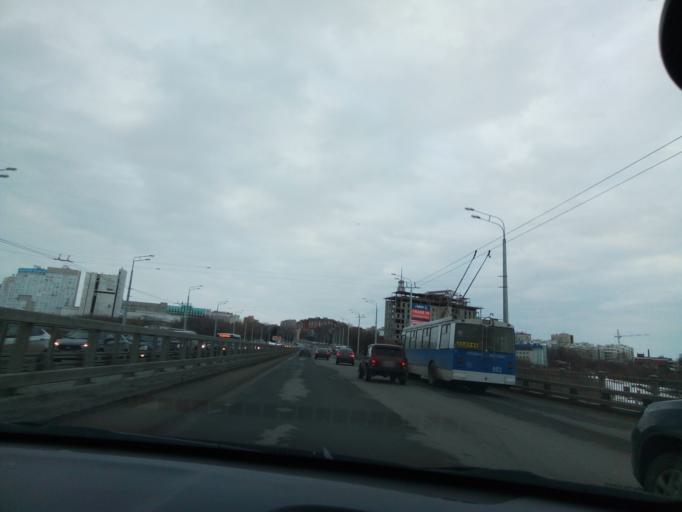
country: RU
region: Chuvashia
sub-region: Cheboksarskiy Rayon
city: Cheboksary
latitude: 56.1445
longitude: 47.2444
